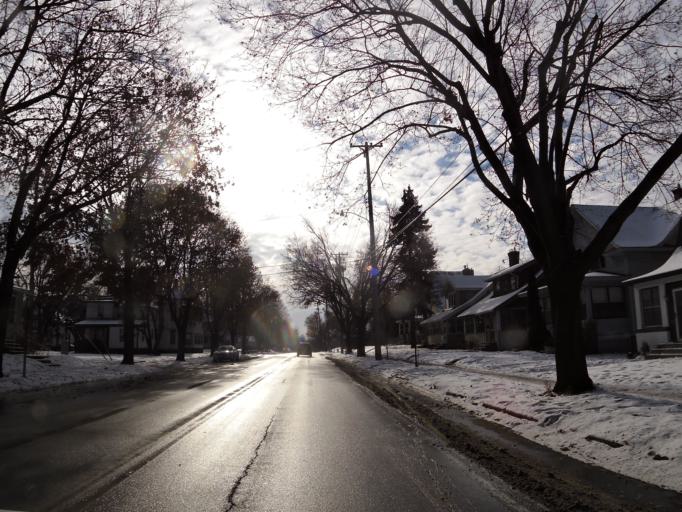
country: US
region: Minnesota
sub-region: Ramsey County
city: Falcon Heights
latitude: 44.9471
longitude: -93.1874
